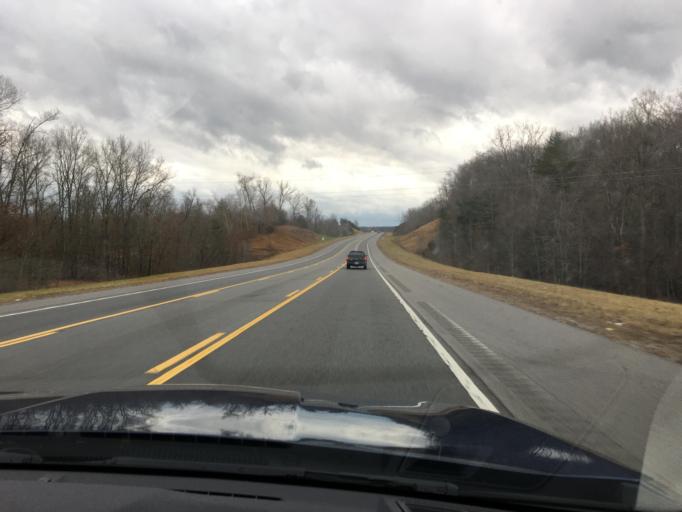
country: US
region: Tennessee
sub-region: Cumberland County
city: Crossville
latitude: 35.9449
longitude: -84.9931
